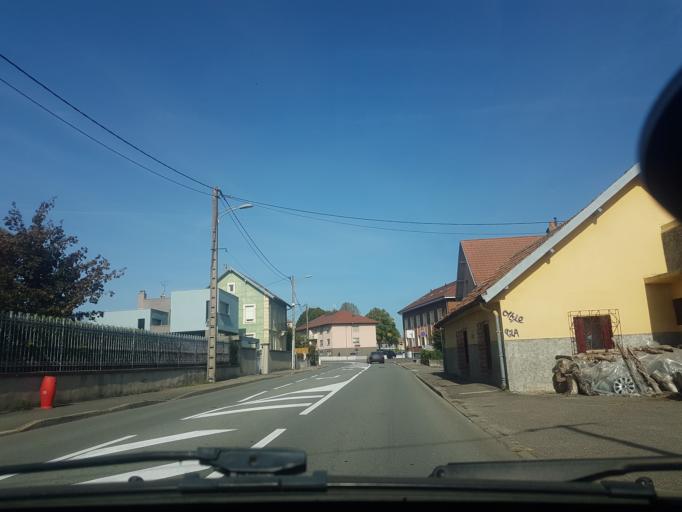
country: FR
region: Franche-Comte
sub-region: Territoire de Belfort
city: Belfort
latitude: 47.6485
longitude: 6.8620
